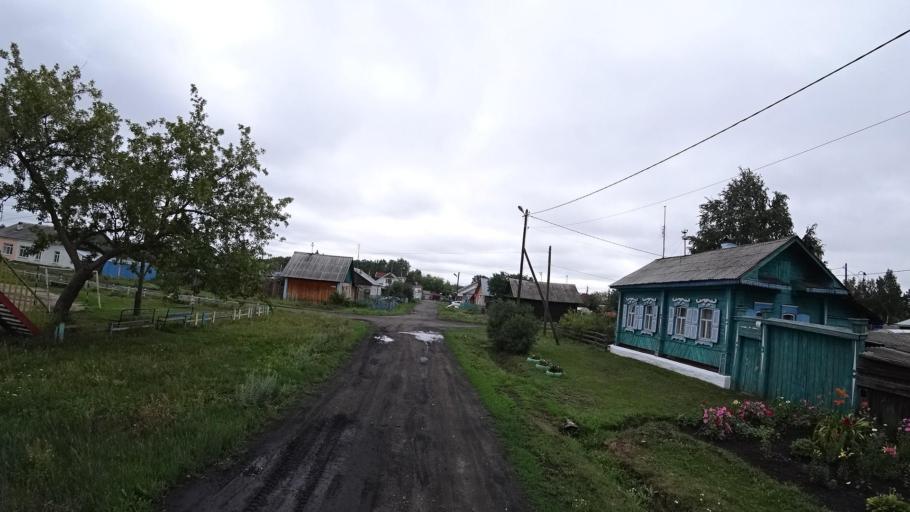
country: RU
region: Sverdlovsk
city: Kamyshlov
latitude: 56.8479
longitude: 62.7641
